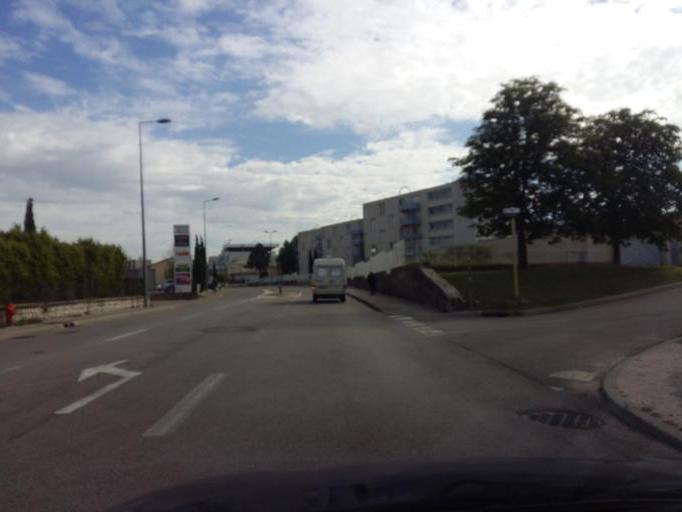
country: FR
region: Languedoc-Roussillon
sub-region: Departement du Gard
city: Bagnols-sur-Ceze
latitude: 44.1567
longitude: 4.6139
